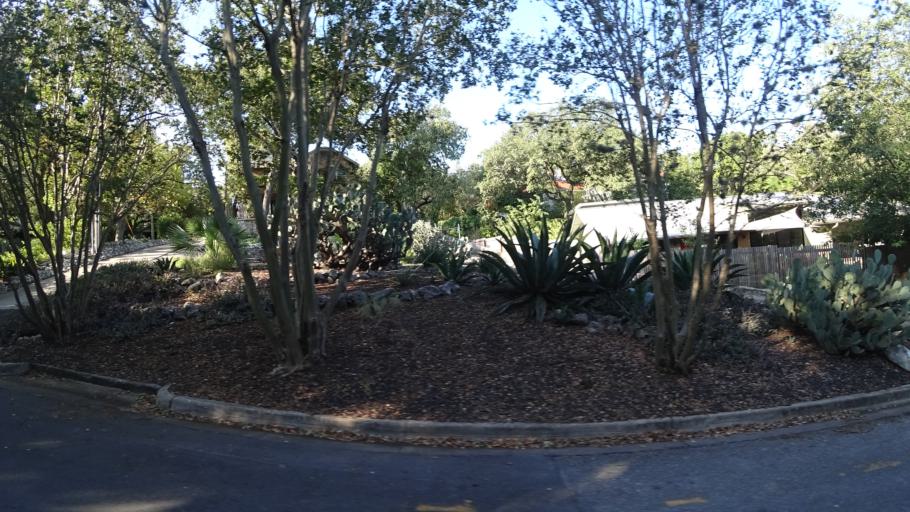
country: US
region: Texas
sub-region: Travis County
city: Austin
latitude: 30.2482
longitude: -97.7401
